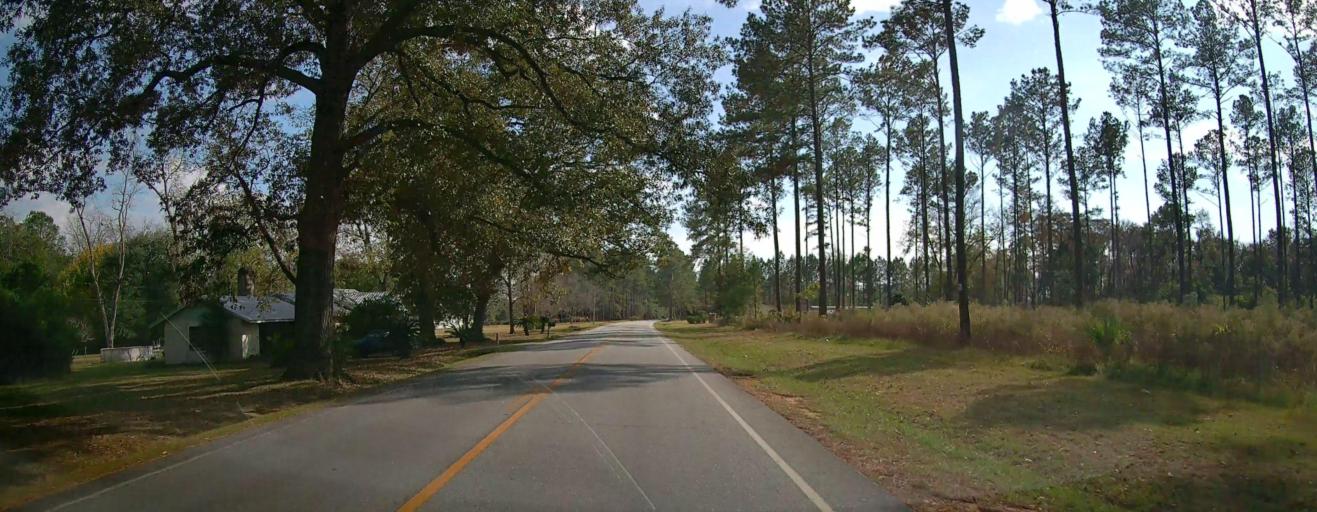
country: US
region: Georgia
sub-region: Thomas County
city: Thomasville
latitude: 30.9477
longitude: -84.0326
